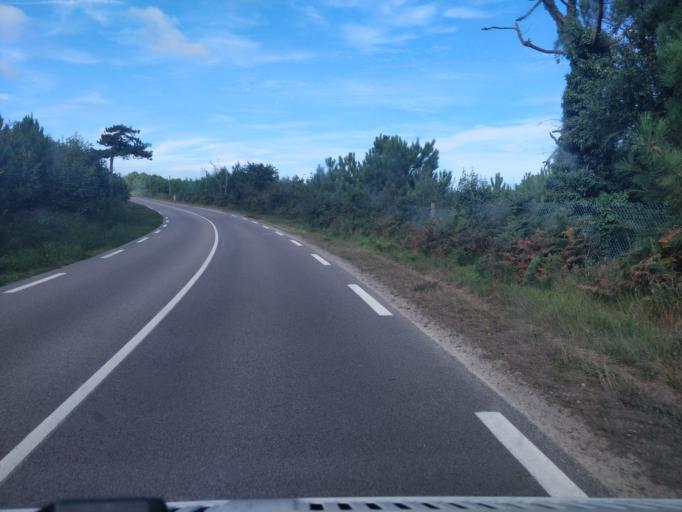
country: FR
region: Brittany
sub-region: Departement des Cotes-d'Armor
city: Plurien
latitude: 48.6489
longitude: -2.3808
